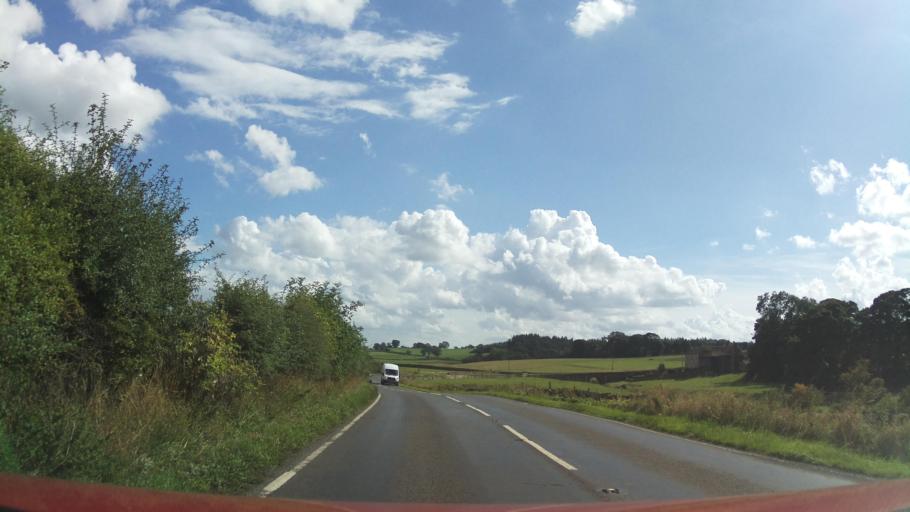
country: GB
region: England
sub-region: North Yorkshire
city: Leyburn
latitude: 54.3617
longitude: -1.8189
